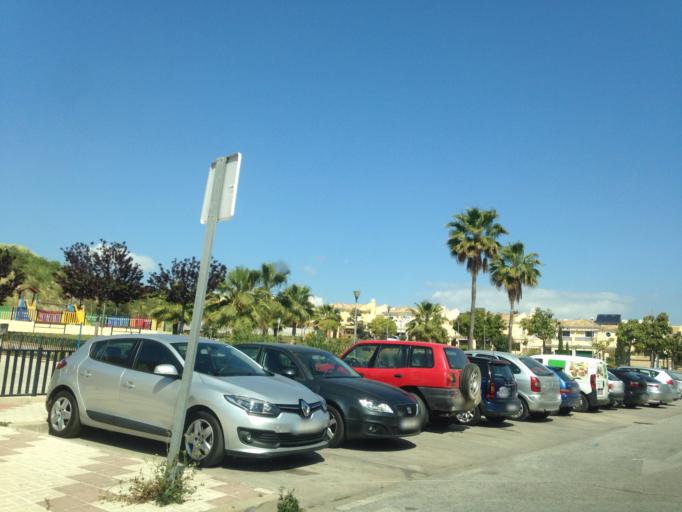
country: ES
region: Andalusia
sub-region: Provincia de Malaga
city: Malaga
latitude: 36.6997
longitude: -4.4744
